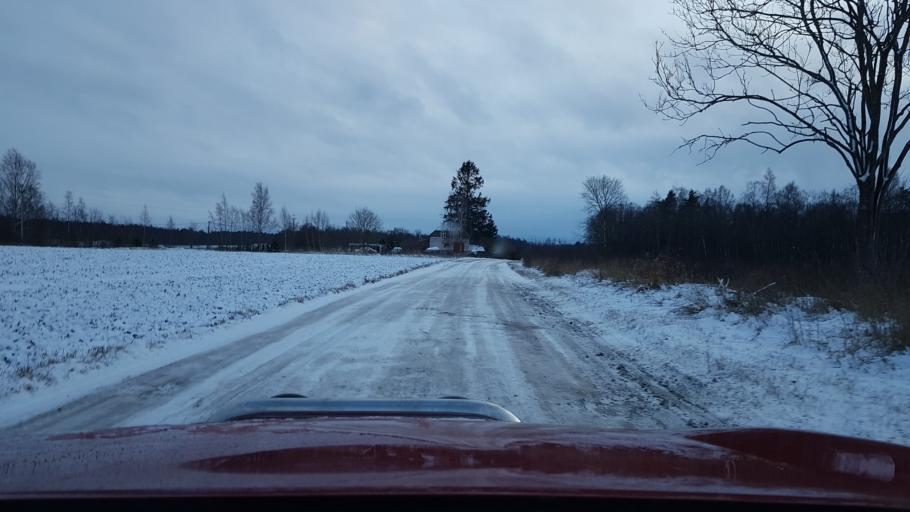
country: EE
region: Harju
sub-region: Maardu linn
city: Maardu
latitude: 59.4199
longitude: 25.0257
